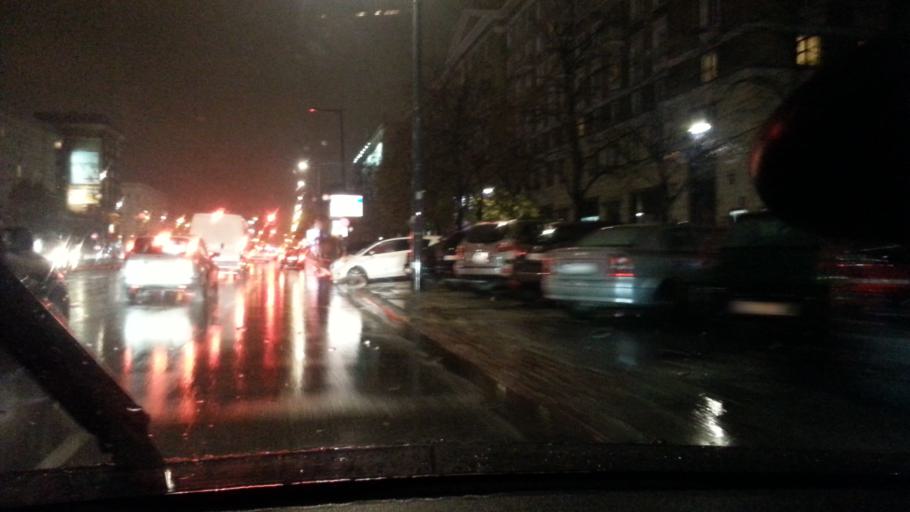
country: PL
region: Masovian Voivodeship
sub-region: Warszawa
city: Wola
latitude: 52.2400
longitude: 20.9956
